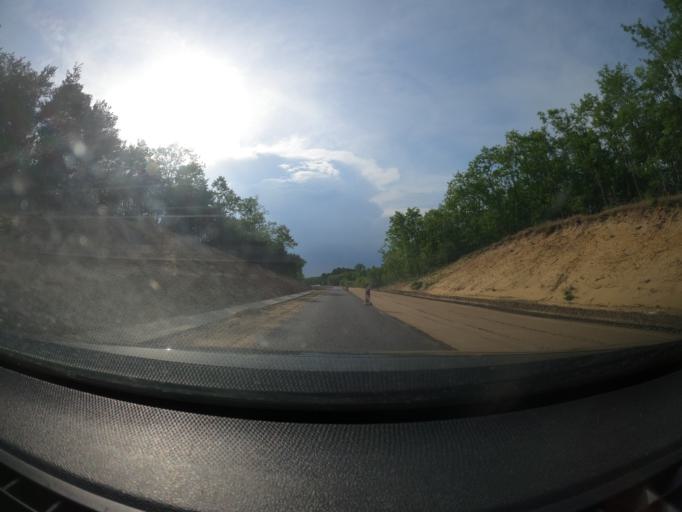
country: HU
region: Hajdu-Bihar
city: Vamospercs
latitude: 47.5248
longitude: 21.8703
